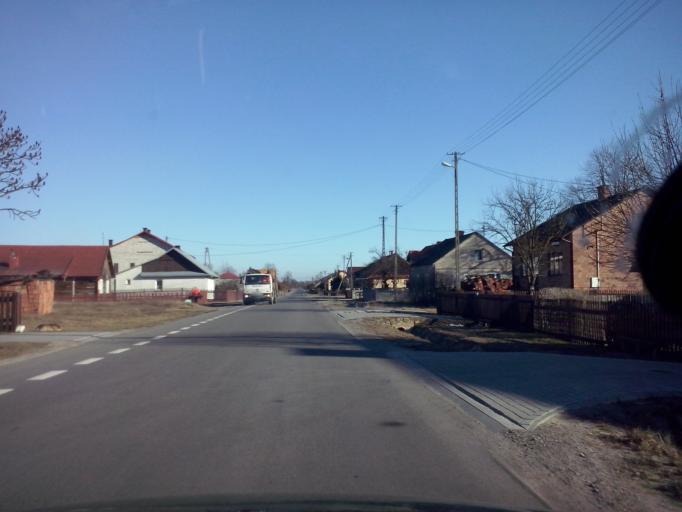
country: PL
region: Subcarpathian Voivodeship
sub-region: Powiat nizanski
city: Harasiuki
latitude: 50.4720
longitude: 22.4924
